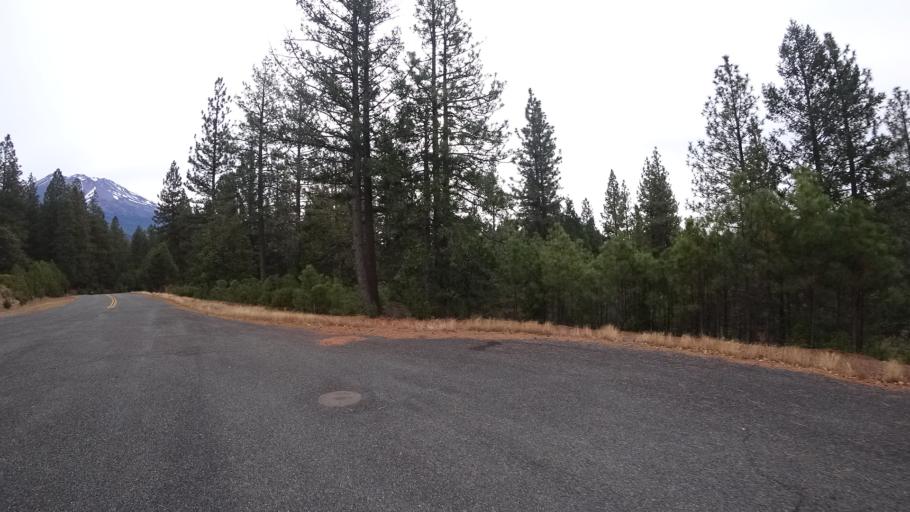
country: US
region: California
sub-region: Siskiyou County
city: Weed
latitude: 41.4134
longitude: -122.3733
